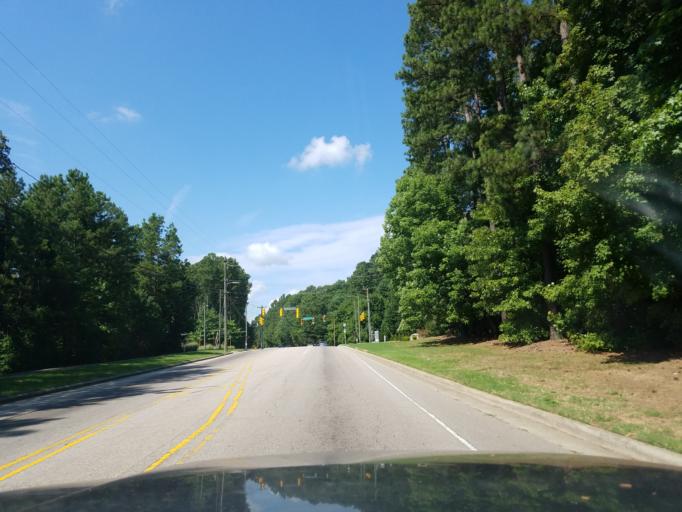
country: US
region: North Carolina
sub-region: Durham County
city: Durham
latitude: 35.9324
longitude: -78.9159
